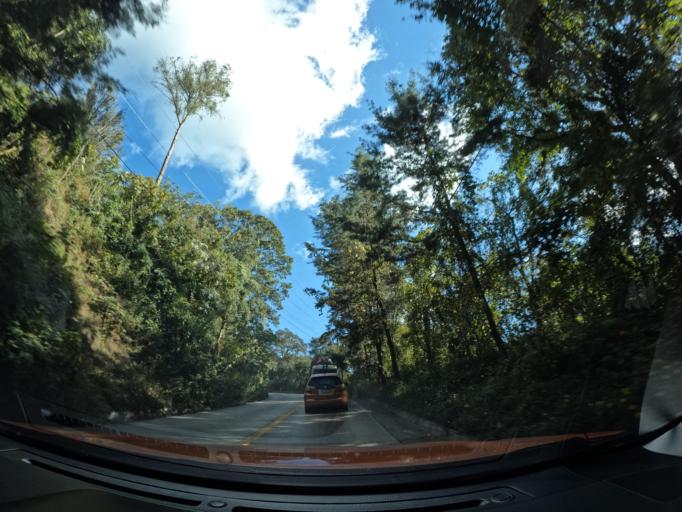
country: GT
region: Sacatepequez
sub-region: Municipio de Santa Maria de Jesus
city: Santa Maria de Jesus
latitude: 14.5079
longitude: -90.7171
